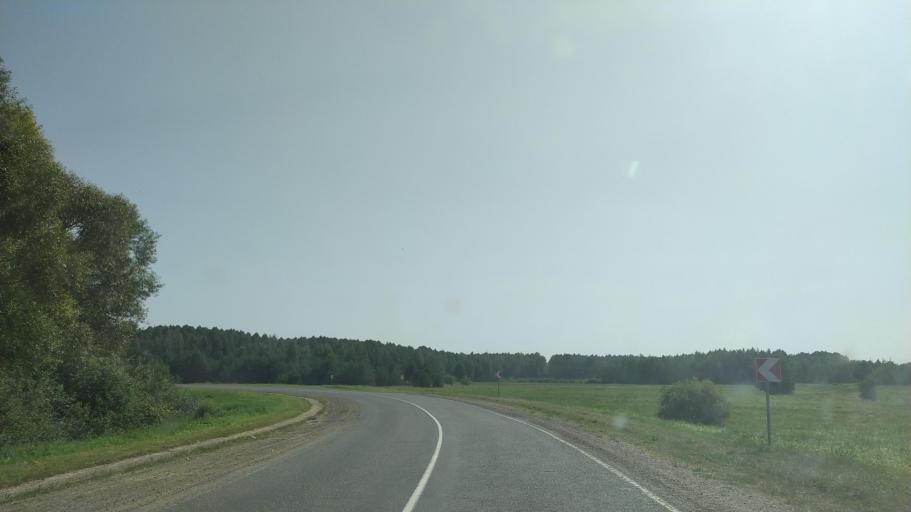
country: BY
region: Brest
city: Byaroza
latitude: 52.4178
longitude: 24.9800
